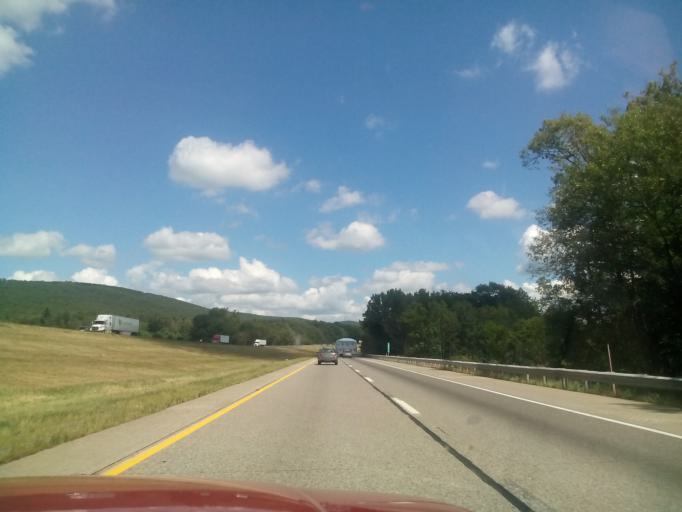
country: US
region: Pennsylvania
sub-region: Luzerne County
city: Conyngham
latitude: 41.0118
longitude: -76.1292
